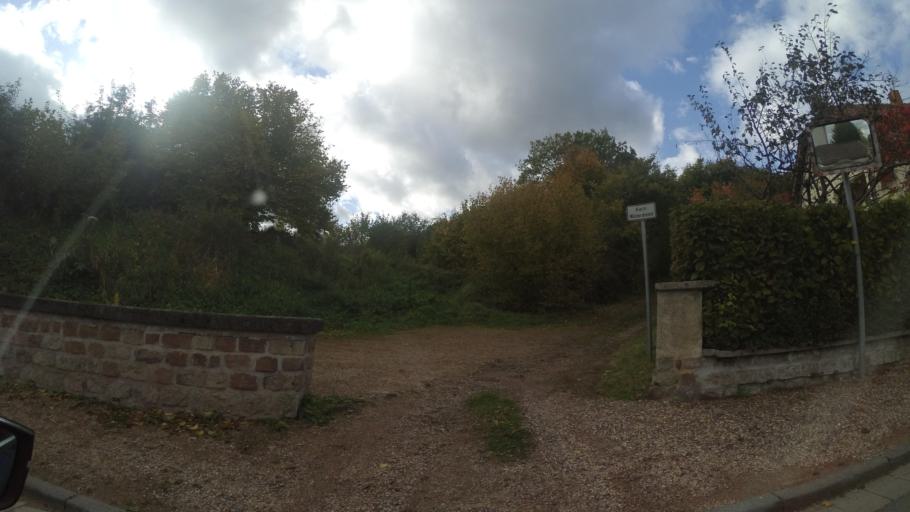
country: DE
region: Saarland
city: Blieskastel
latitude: 49.2380
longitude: 7.2527
